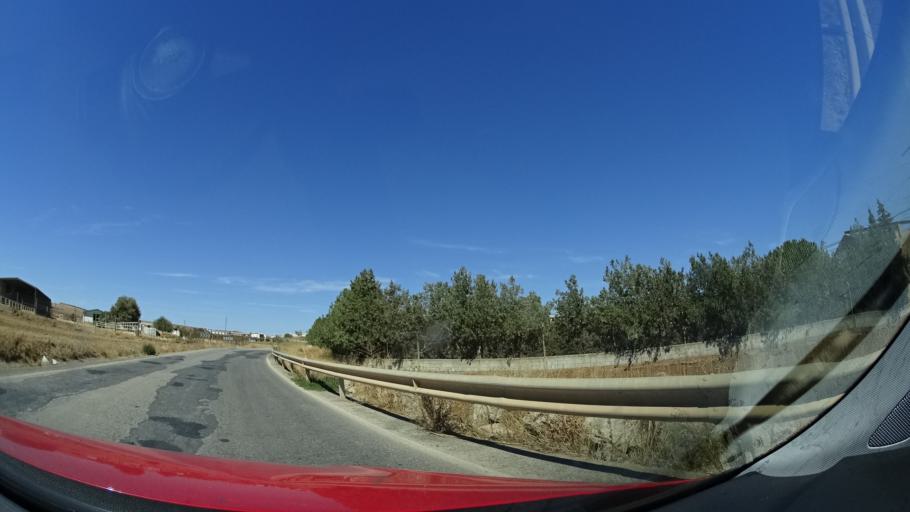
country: ES
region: Andalusia
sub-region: Provincia de Malaga
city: Campillos
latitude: 37.0573
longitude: -4.8643
